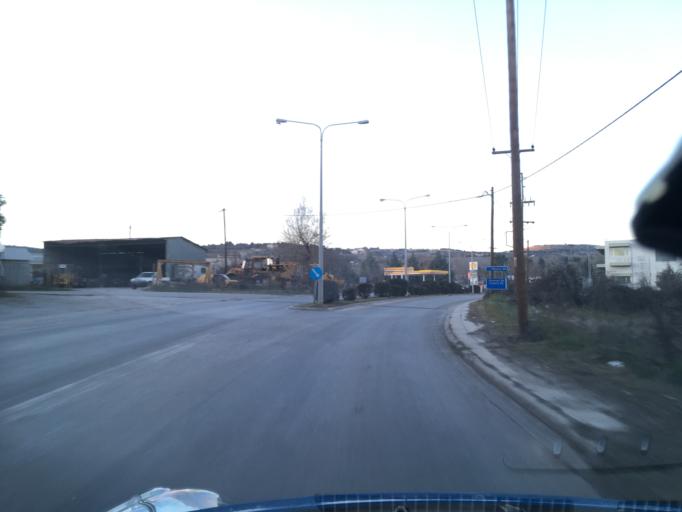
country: GR
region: West Macedonia
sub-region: Nomos Kozanis
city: Kozani
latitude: 40.2852
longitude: 21.7785
